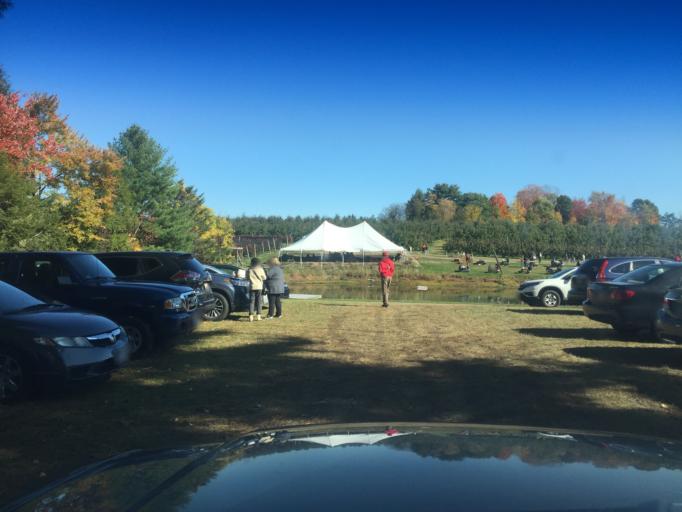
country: US
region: Massachusetts
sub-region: Middlesex County
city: Stow
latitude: 42.4097
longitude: -71.5182
